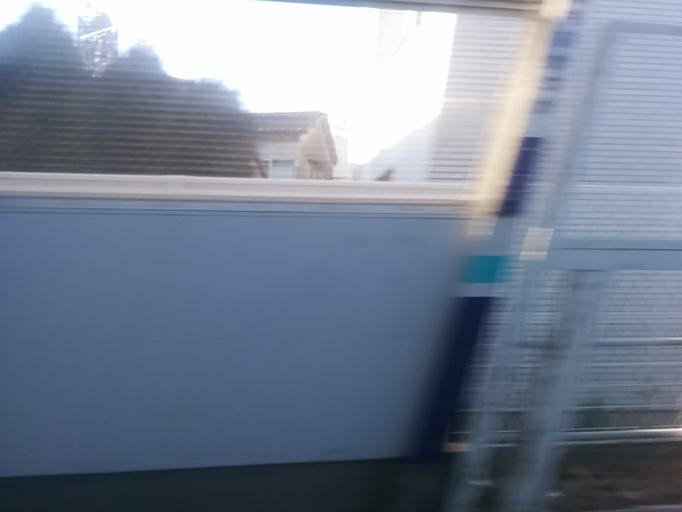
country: JP
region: Saitama
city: Wako
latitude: 35.7709
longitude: 139.6438
